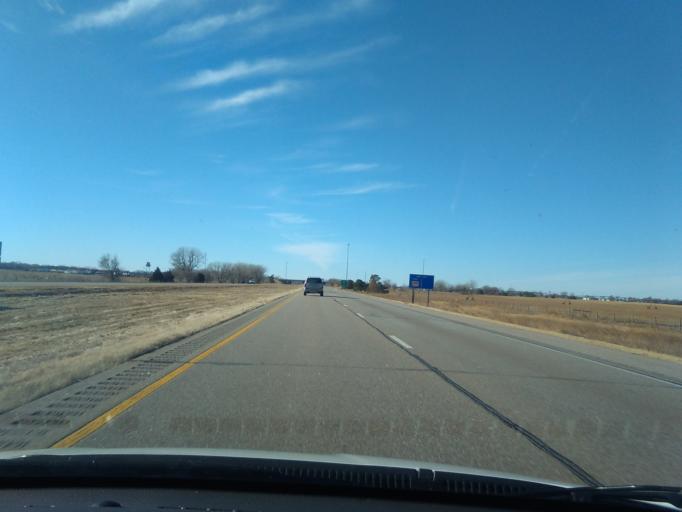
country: US
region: Nebraska
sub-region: Hall County
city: Wood River
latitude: 40.7660
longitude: -98.5776
